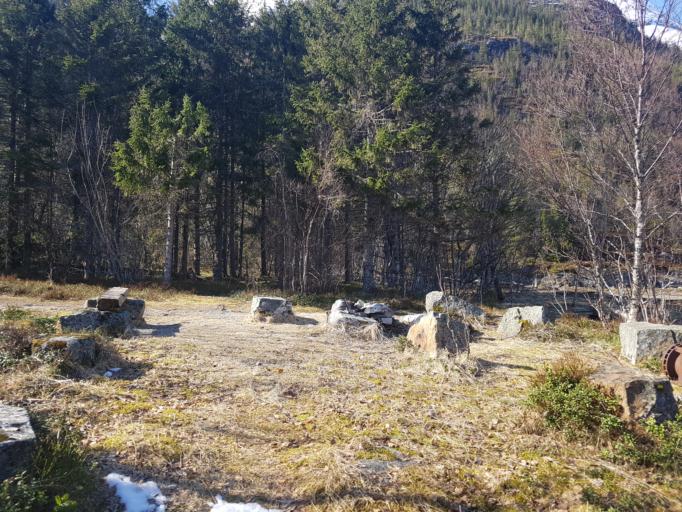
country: NO
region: Nordland
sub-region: Vefsn
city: Mosjoen
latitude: 65.8440
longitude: 13.1785
